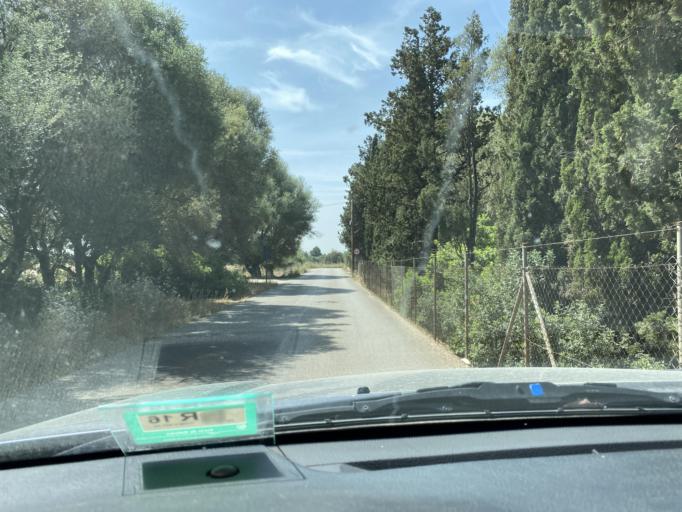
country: ES
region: Balearic Islands
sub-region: Illes Balears
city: Marratxi
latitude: 39.6271
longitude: 2.7112
